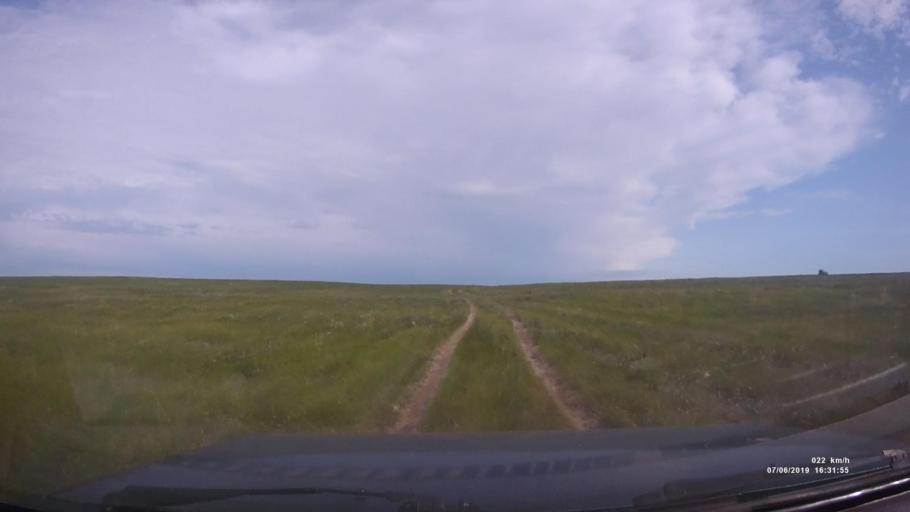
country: RU
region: Rostov
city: Staraya Stanitsa
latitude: 48.2549
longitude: 40.3283
